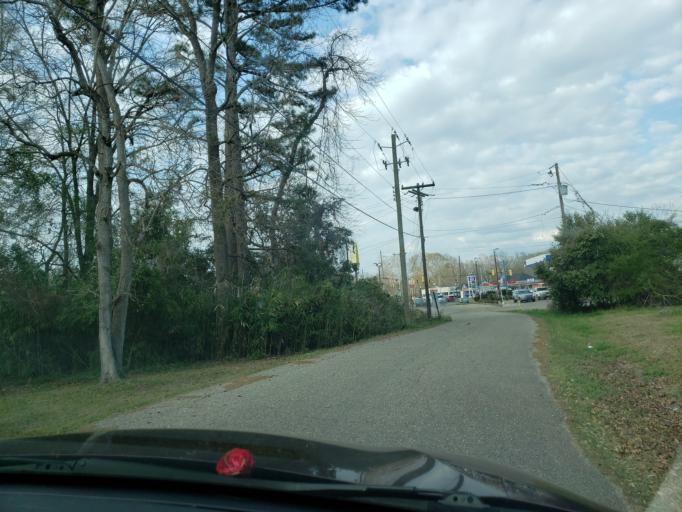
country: US
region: Alabama
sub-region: Hale County
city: Greensboro
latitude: 32.6984
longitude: -87.5958
